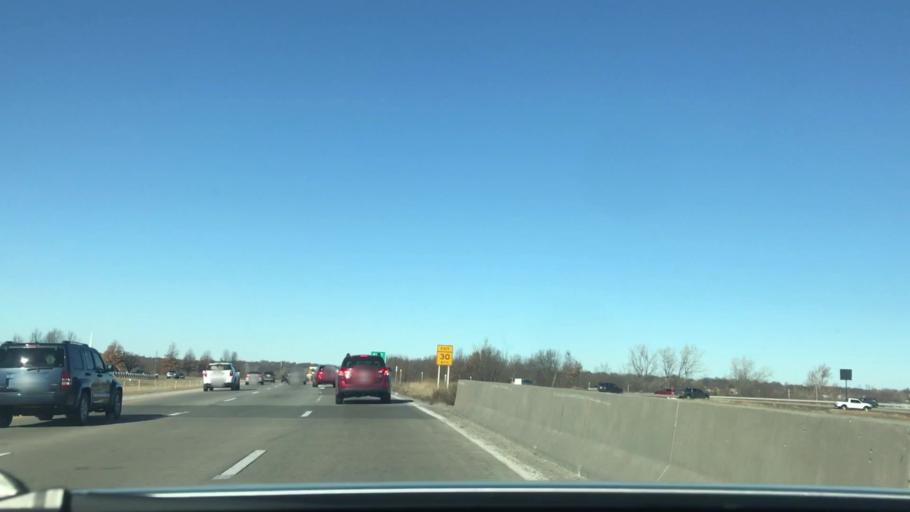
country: US
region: Missouri
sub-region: Jackson County
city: East Independence
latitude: 39.0483
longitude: -94.3637
